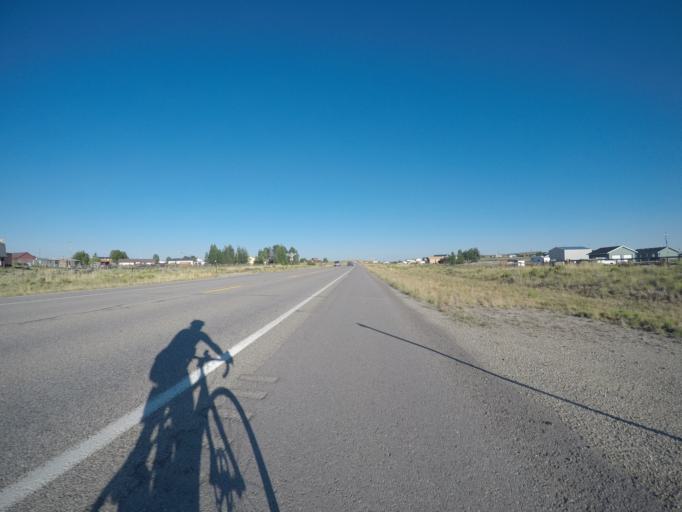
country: US
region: Wyoming
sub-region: Sublette County
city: Pinedale
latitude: 42.8795
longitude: -109.9676
